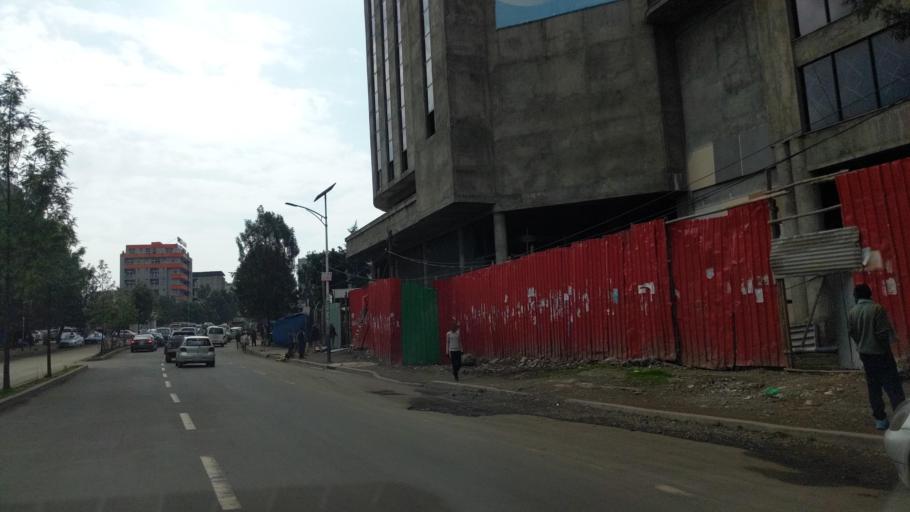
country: ET
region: Adis Abeba
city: Addis Ababa
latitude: 9.0029
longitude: 38.7989
